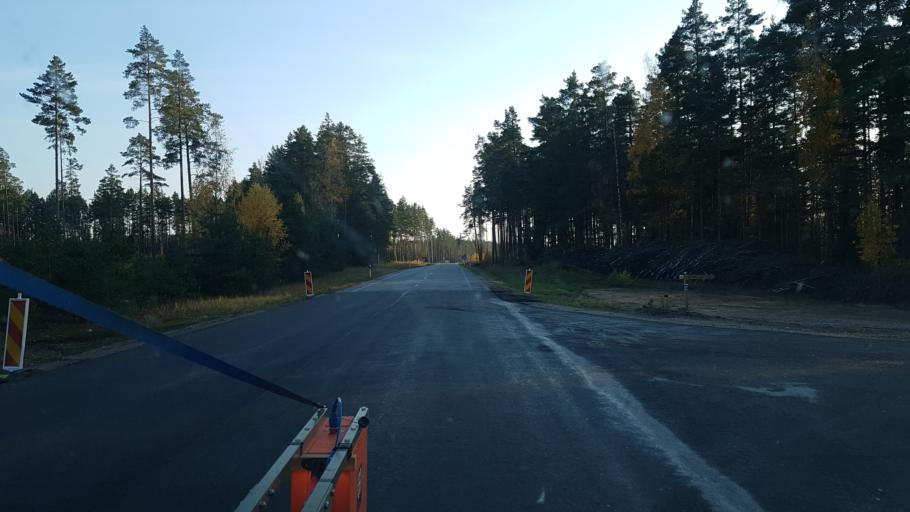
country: EE
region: Polvamaa
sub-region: Polva linn
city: Polva
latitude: 57.9256
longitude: 27.1825
